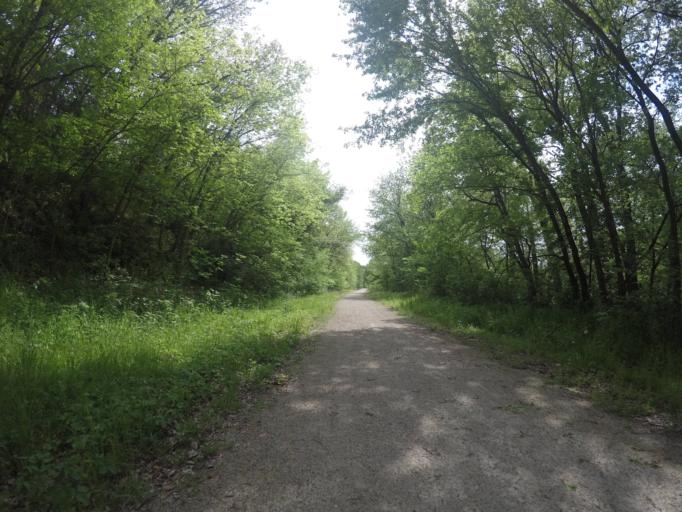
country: US
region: Kansas
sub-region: Marshall County
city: Marysville
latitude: 39.9654
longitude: -96.6022
